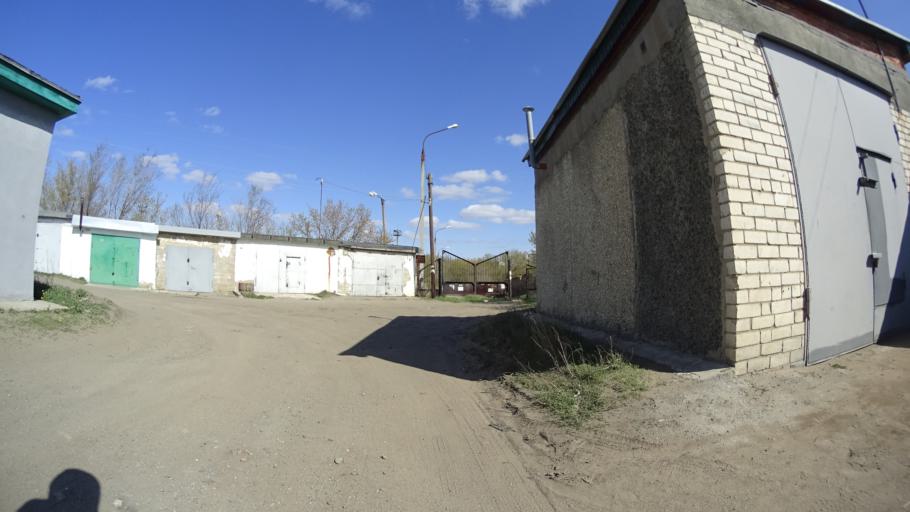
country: RU
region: Chelyabinsk
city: Troitsk
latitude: 54.0826
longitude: 61.5297
